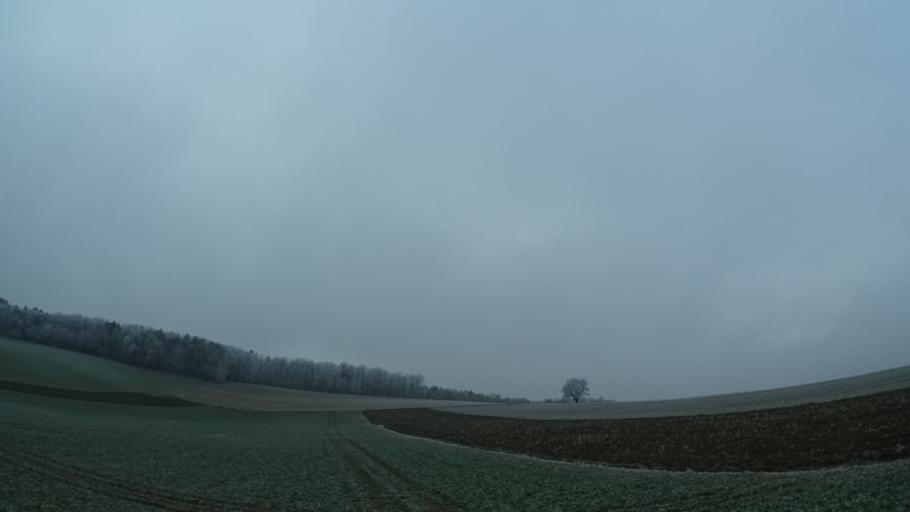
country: DE
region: Baden-Wuerttemberg
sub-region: Regierungsbezirk Stuttgart
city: Boxberg
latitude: 49.5172
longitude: 9.6340
